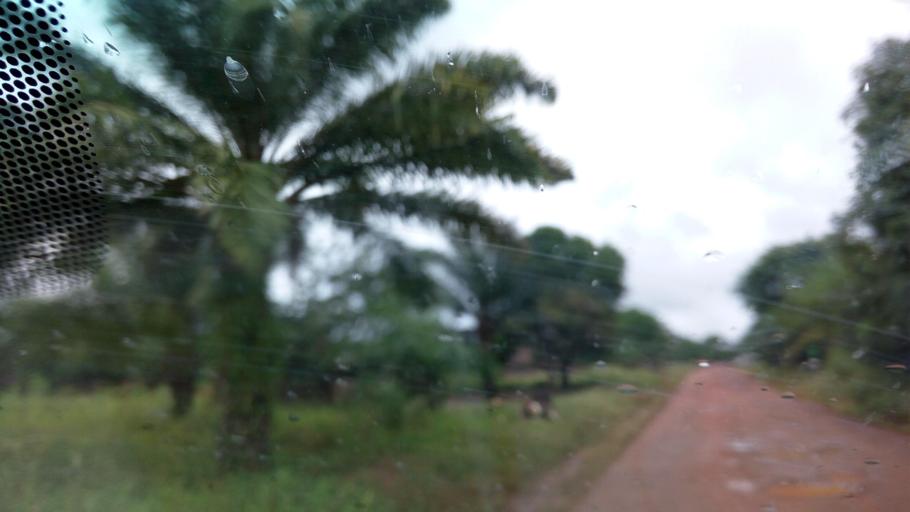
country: ZM
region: Luapula
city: Nchelenge
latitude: -9.1331
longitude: 28.2987
